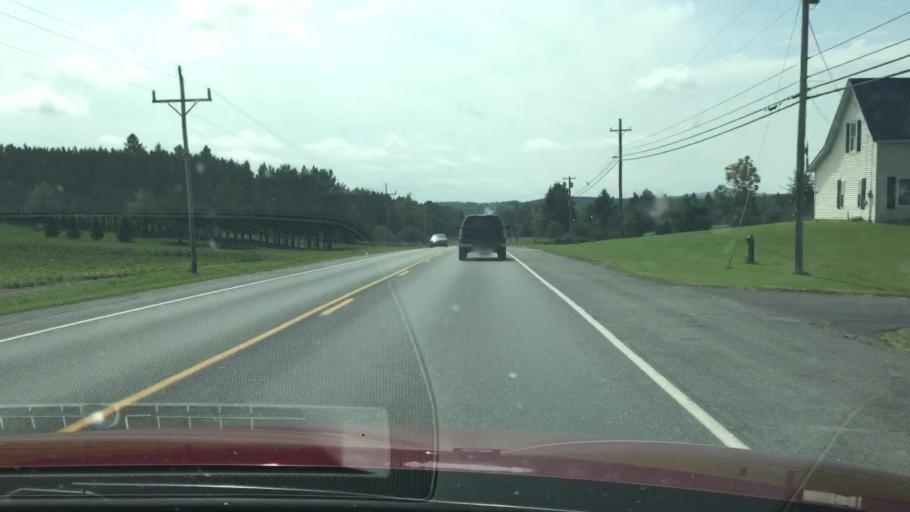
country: US
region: Maine
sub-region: Aroostook County
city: Easton
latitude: 46.4895
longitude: -67.8685
